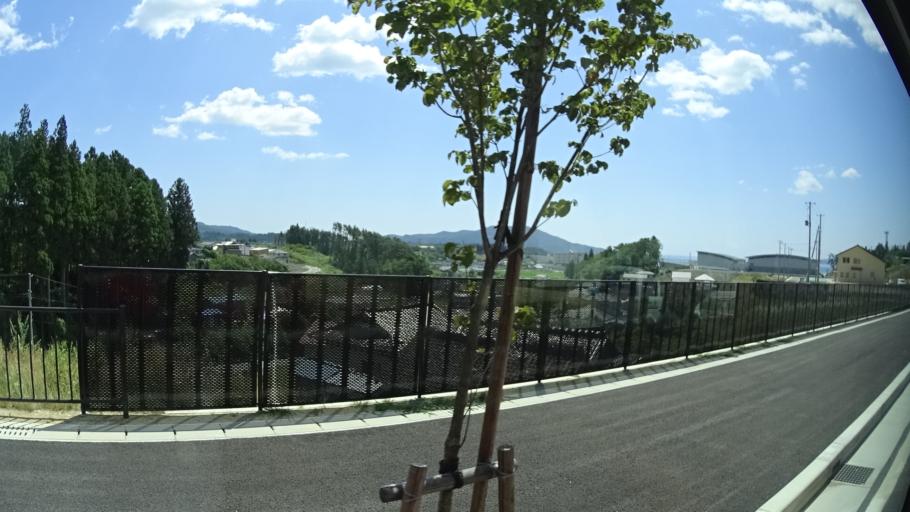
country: JP
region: Iwate
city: Ofunato
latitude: 39.0213
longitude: 141.6399
